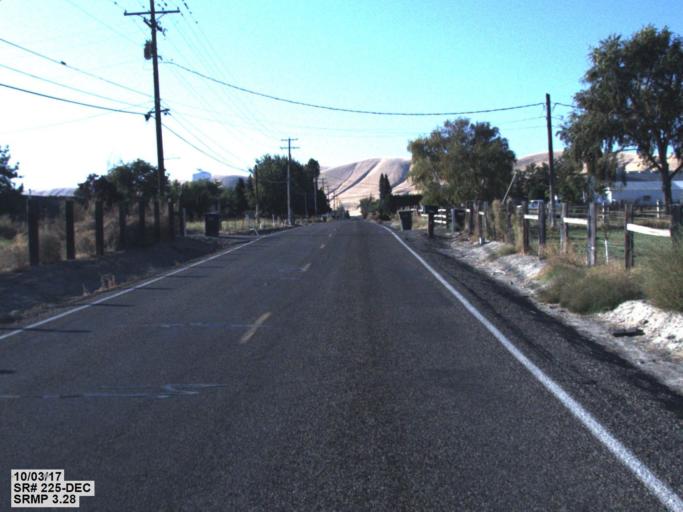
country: US
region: Washington
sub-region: Benton County
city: Benton City
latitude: 46.2907
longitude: -119.4939
